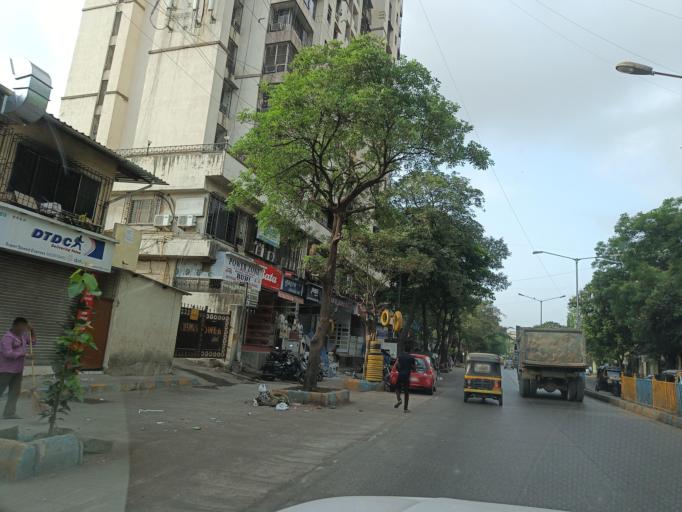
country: IN
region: Maharashtra
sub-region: Thane
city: Thane
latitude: 19.2112
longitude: 72.9773
